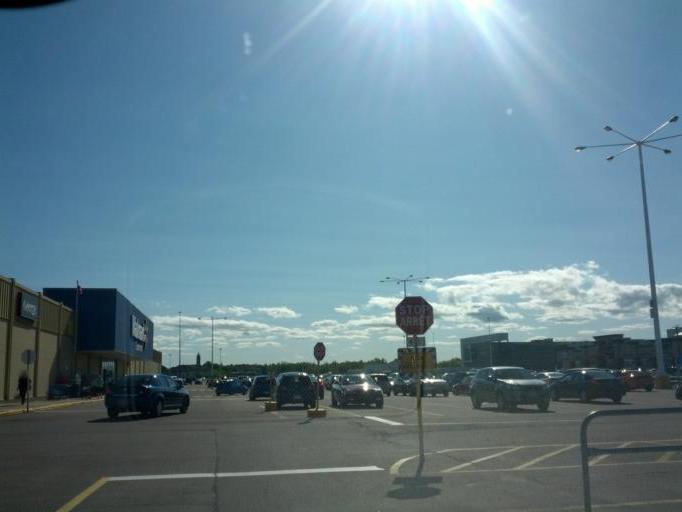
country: CA
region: New Brunswick
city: Moncton
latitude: 46.0979
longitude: -64.7600
